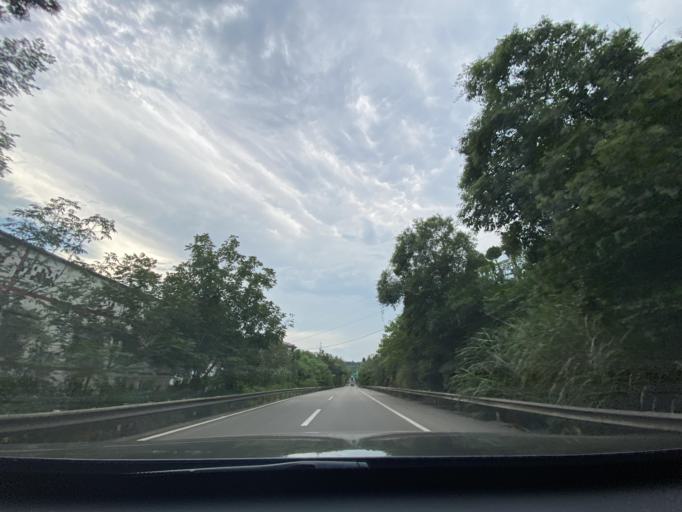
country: CN
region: Sichuan
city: Neijiang
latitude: 29.6792
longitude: 104.9624
